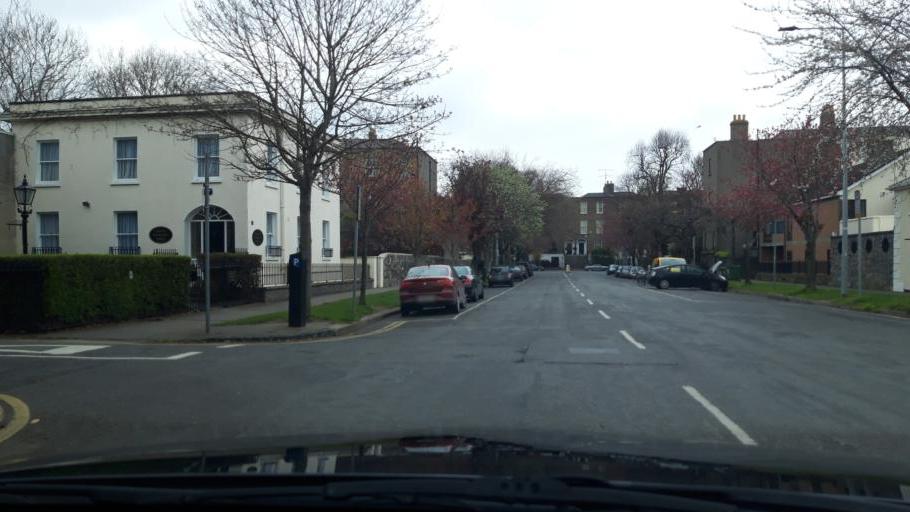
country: IE
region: Leinster
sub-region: Dublin City
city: Dublin
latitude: 53.3315
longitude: -6.2408
